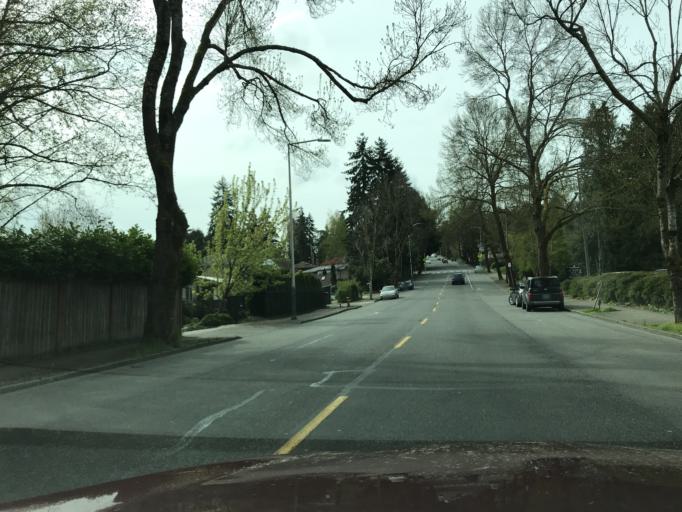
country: US
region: Washington
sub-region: King County
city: Lake Forest Park
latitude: 47.7063
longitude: -122.2909
